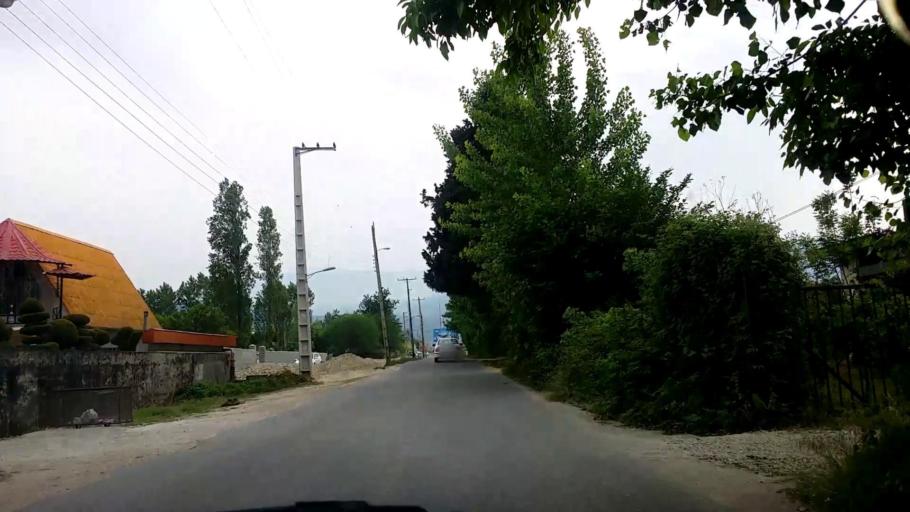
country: IR
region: Mazandaran
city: Chalus
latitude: 36.6847
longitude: 51.4043
